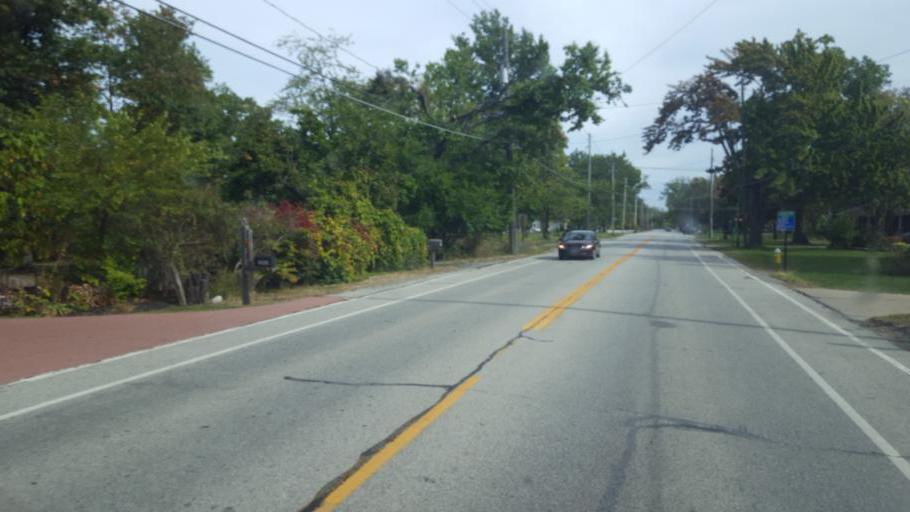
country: US
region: Ohio
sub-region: Lorain County
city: Avon Lake
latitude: 41.5113
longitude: -81.9901
